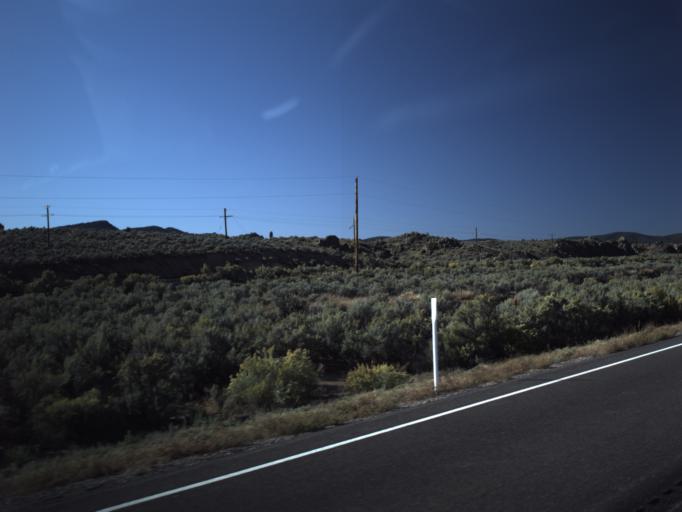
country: US
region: Utah
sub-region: Washington County
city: Enterprise
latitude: 37.7467
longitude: -114.0063
